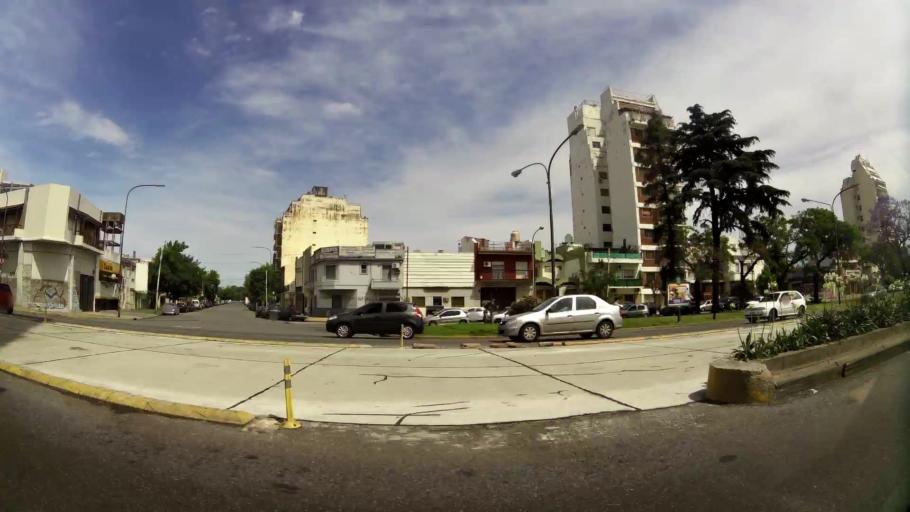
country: AR
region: Buenos Aires F.D.
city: Villa Santa Rita
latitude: -34.6317
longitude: -58.5001
